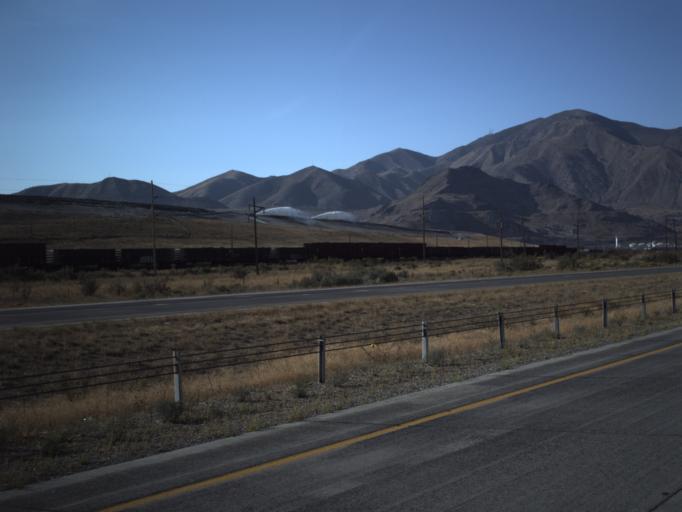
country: US
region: Utah
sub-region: Salt Lake County
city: Magna
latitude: 40.7575
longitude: -112.1685
